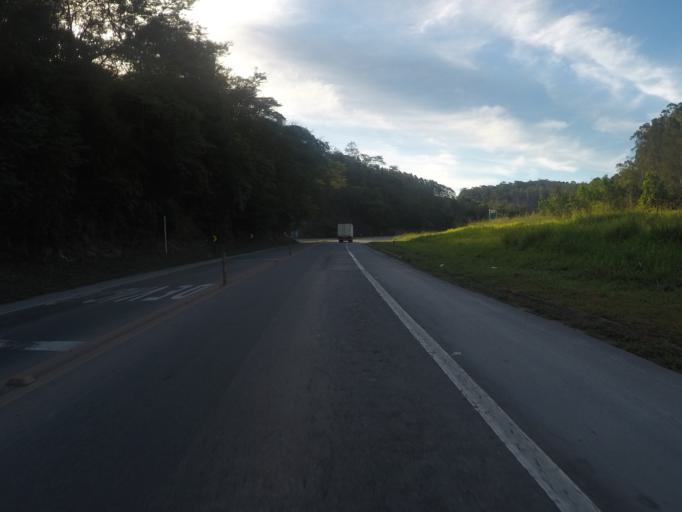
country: BR
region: Espirito Santo
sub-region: Ibiracu
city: Ibiracu
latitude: -19.8346
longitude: -40.3805
